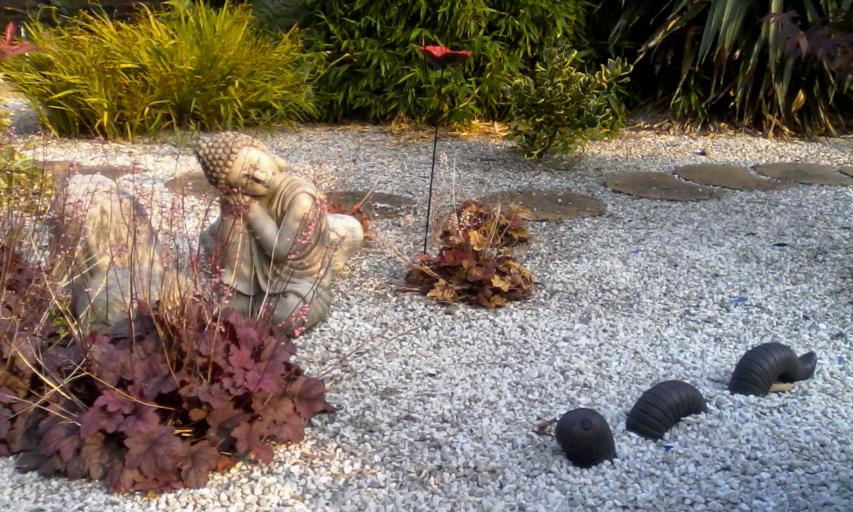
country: GB
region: England
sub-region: Nottinghamshire
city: Arnold
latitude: 52.9715
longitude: -1.0944
